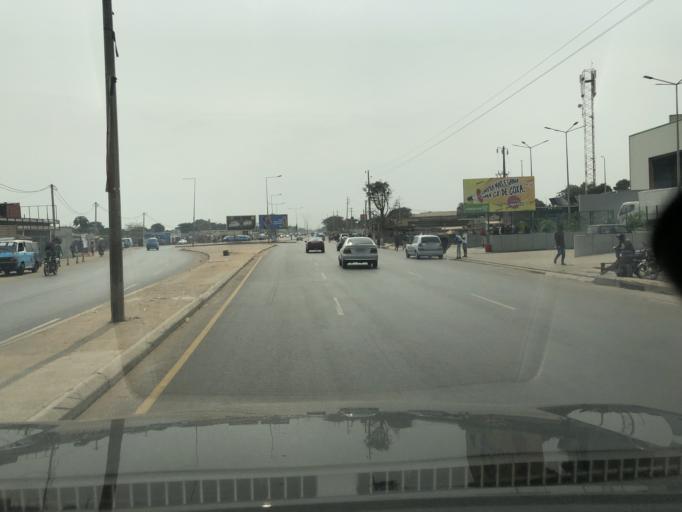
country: AO
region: Luanda
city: Luanda
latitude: -8.7995
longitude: 13.3143
